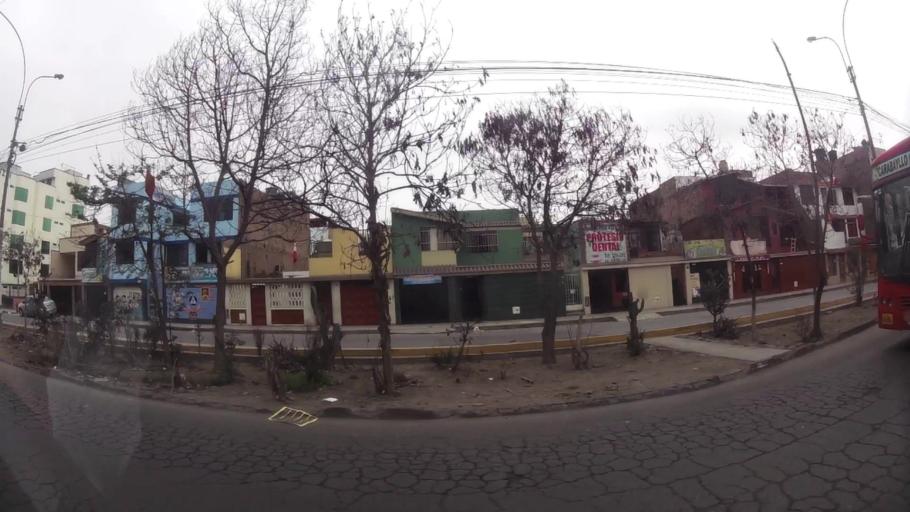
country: PE
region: Lima
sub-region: Lima
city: Independencia
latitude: -12.0050
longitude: -77.0835
